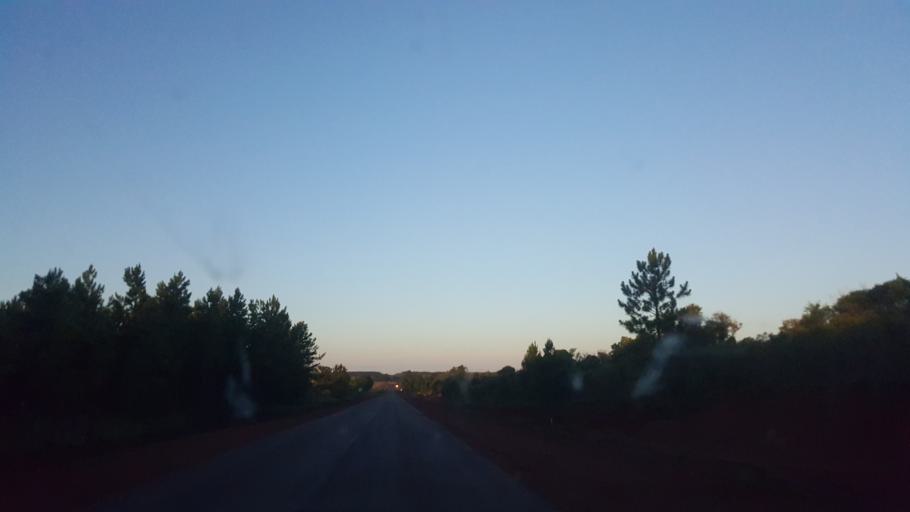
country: AR
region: Corrientes
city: Santo Tome
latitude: -28.3937
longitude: -55.9704
